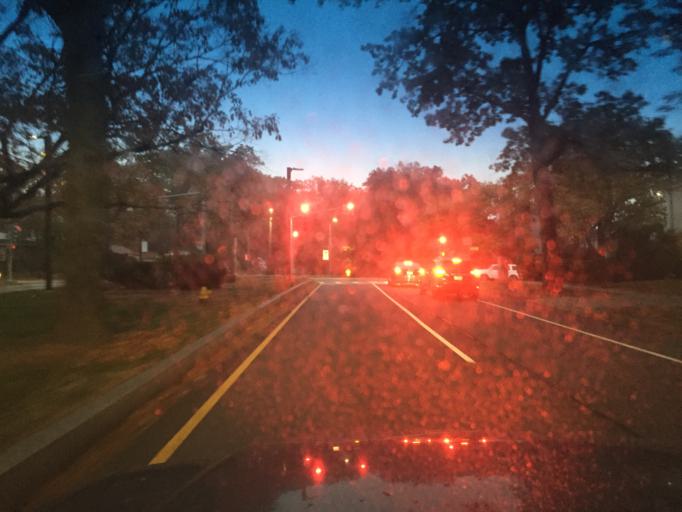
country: US
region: Massachusetts
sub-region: Suffolk County
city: Jamaica Plain
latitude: 42.2959
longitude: -71.1512
